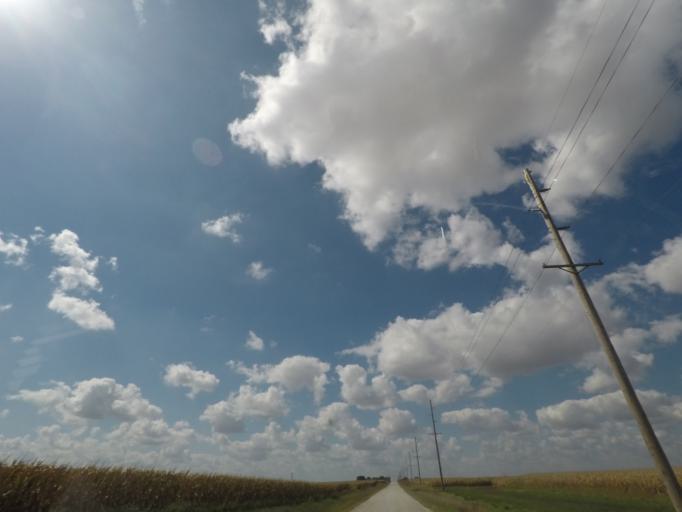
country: US
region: Iowa
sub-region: Story County
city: Nevada
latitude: 42.0344
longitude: -93.3972
